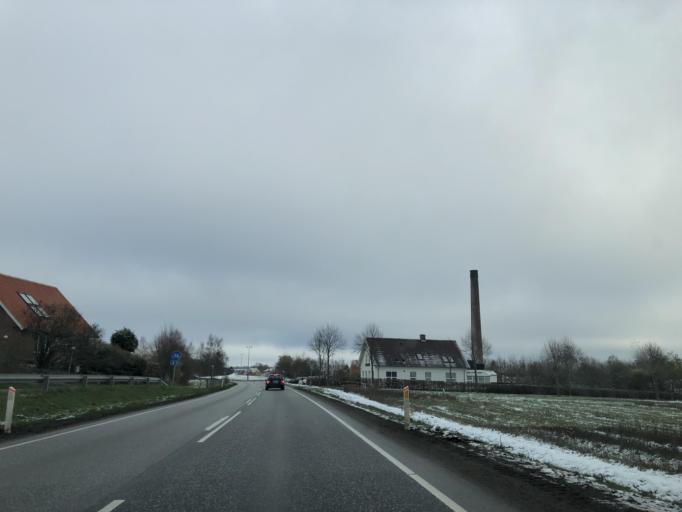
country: DK
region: Central Jutland
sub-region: Horsens Kommune
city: Horsens
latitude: 55.8961
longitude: 9.7500
